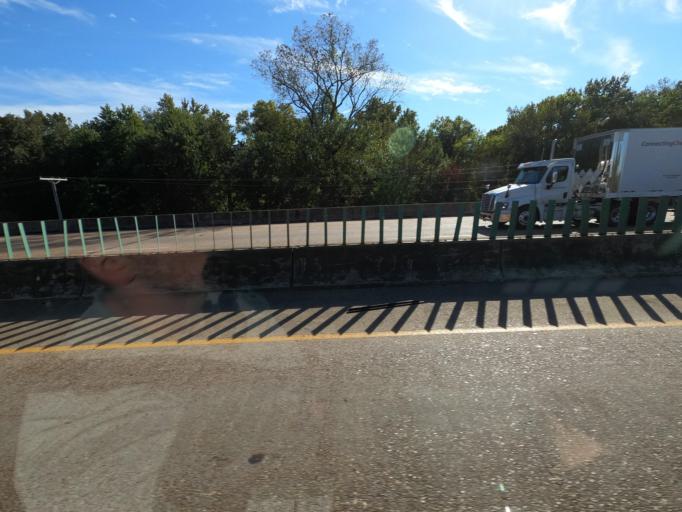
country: US
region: Tennessee
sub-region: Shelby County
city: Memphis
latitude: 35.1387
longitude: -90.0980
